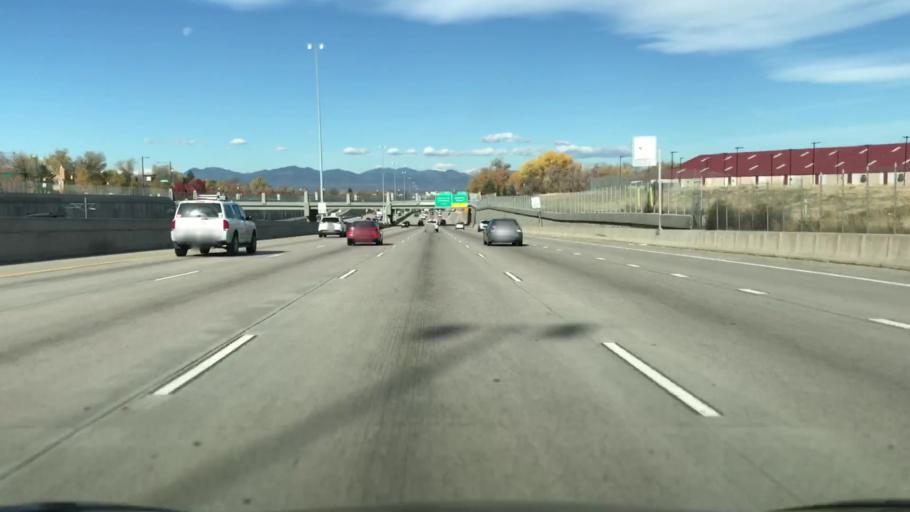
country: US
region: Colorado
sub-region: Arapahoe County
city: Glendale
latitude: 39.6865
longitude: -104.9662
